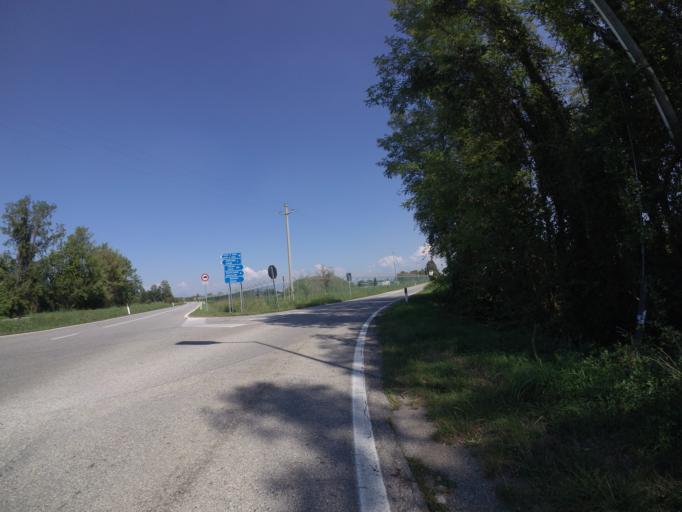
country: IT
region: Friuli Venezia Giulia
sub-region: Provincia di Udine
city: Codroipo
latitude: 45.9827
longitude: 12.9939
